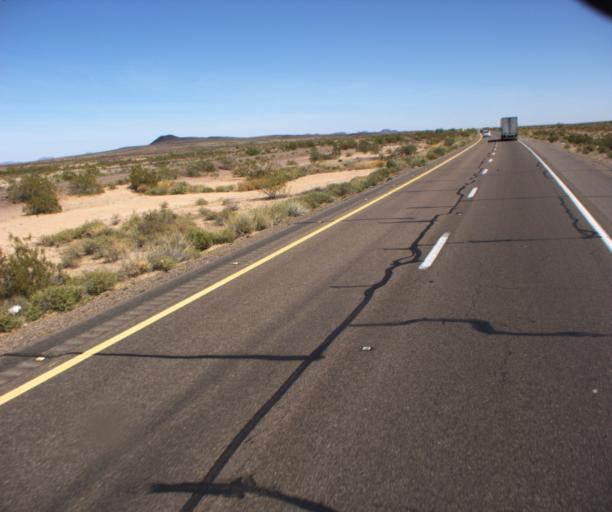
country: US
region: Arizona
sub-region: Maricopa County
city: Gila Bend
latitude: 32.8629
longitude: -113.1676
